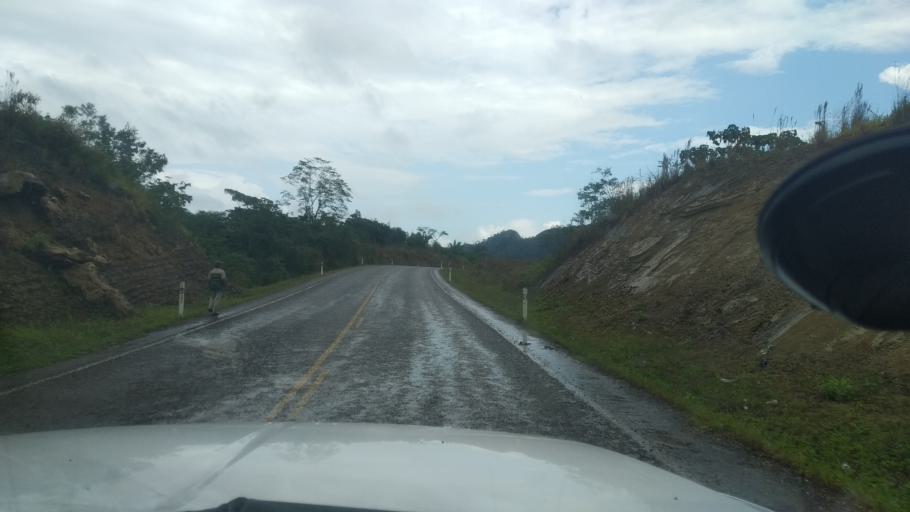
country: GT
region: Peten
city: San Luis
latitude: 16.1840
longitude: -89.2035
